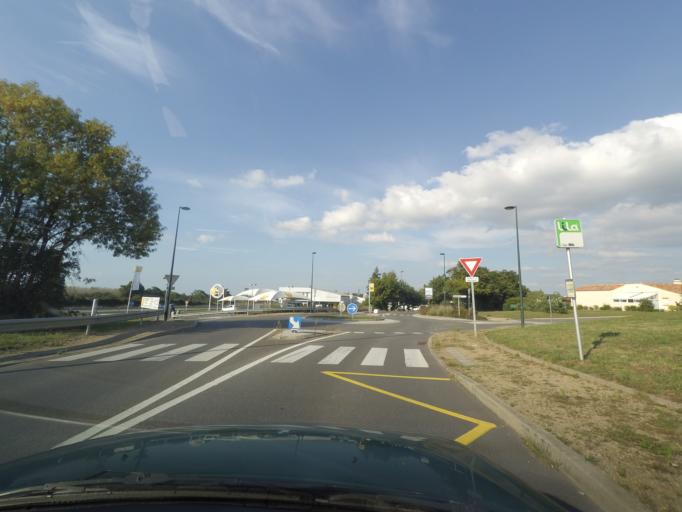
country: FR
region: Pays de la Loire
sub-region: Departement de la Loire-Atlantique
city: Saint-Philbert-de-Grand-Lieu
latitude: 47.0344
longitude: -1.6550
